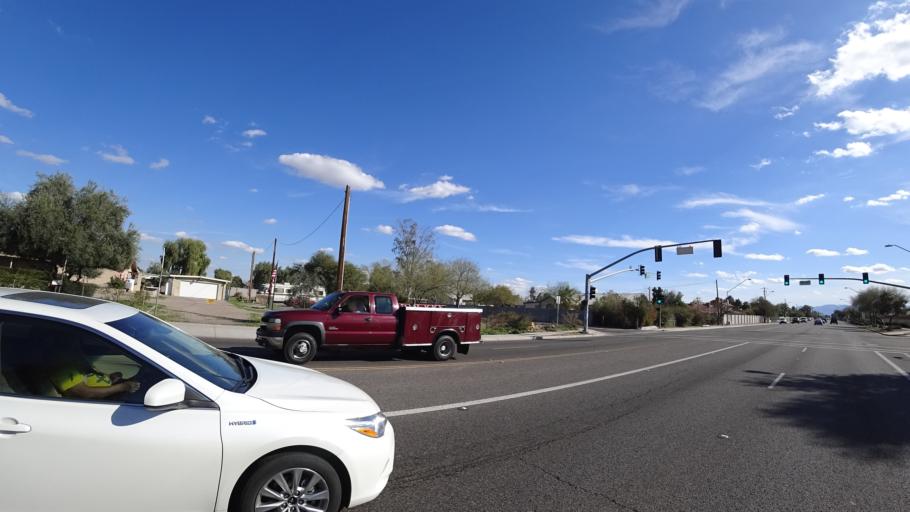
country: US
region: Arizona
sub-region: Maricopa County
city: Glendale
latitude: 33.5167
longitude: -112.2206
